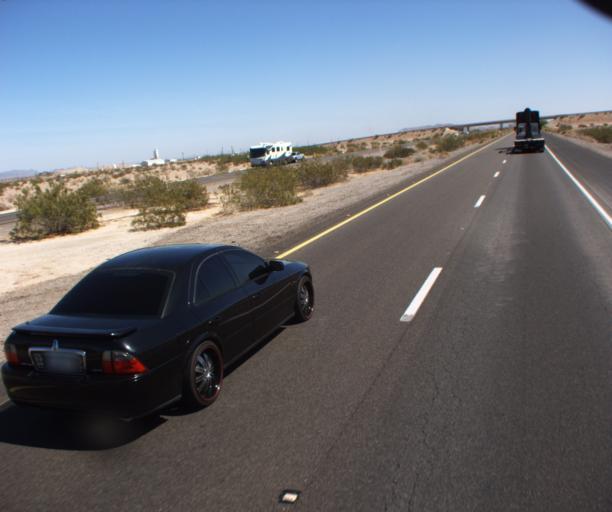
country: US
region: Arizona
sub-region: Yuma County
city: Wellton
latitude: 32.6687
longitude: -114.1127
